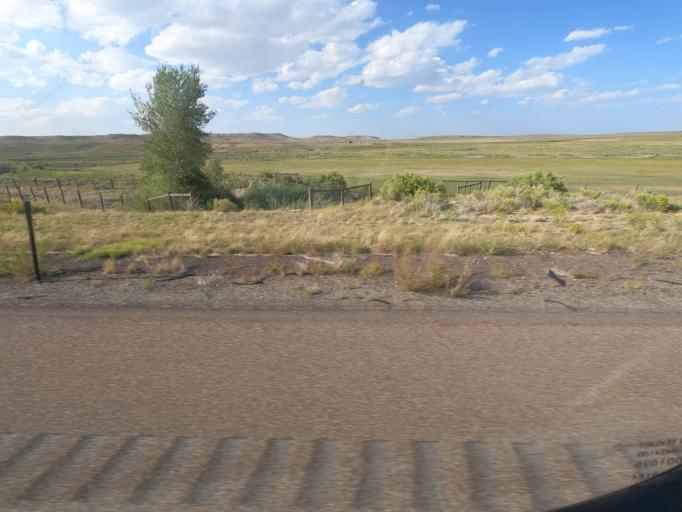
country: US
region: Wyoming
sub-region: Uinta County
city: Lyman
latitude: 41.3550
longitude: -110.3638
